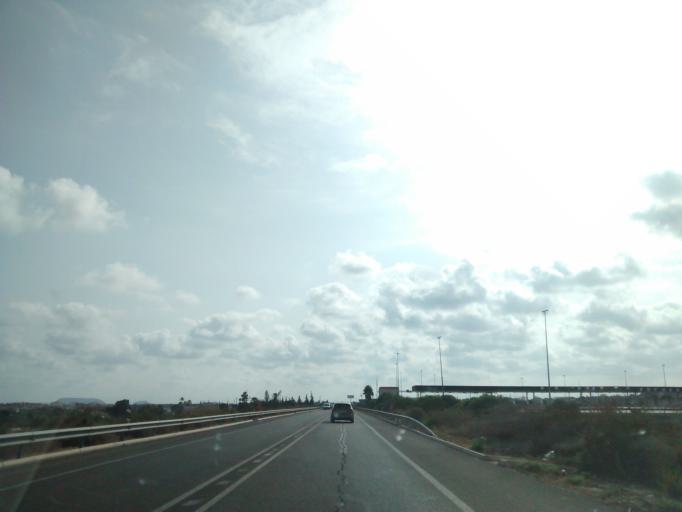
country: ES
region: Valencia
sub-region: Provincia de Alicante
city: el Campello
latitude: 38.4408
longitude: -0.3971
